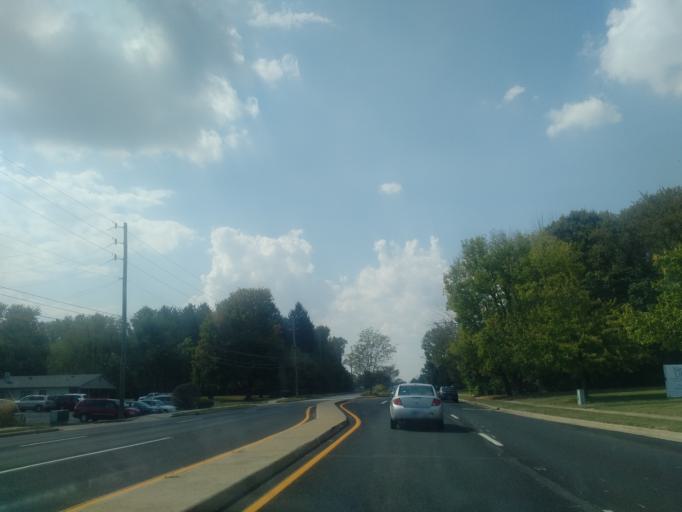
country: US
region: Indiana
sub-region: Marion County
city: Meridian Hills
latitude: 39.9122
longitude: -86.1868
